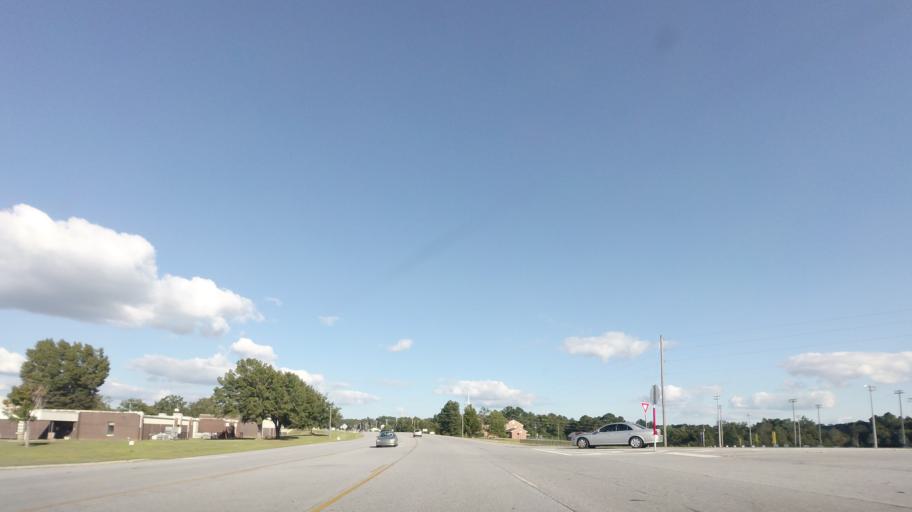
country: US
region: Georgia
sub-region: Lamar County
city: Barnesville
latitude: 33.0467
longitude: -84.1770
